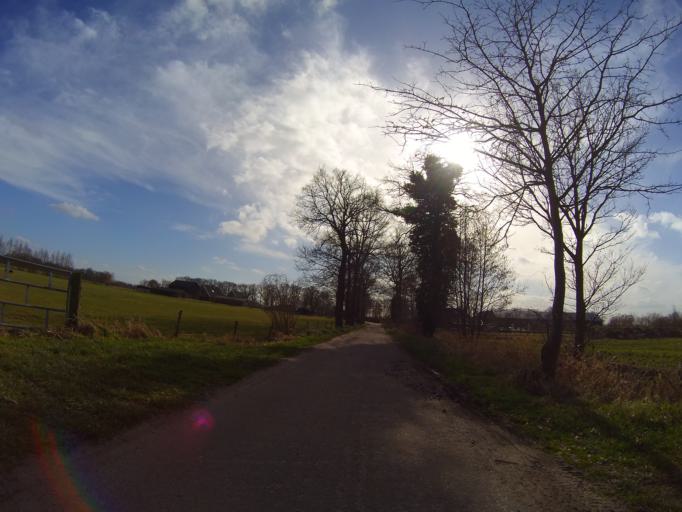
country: NL
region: Gelderland
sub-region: Gemeente Barneveld
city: Zwartebroek
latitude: 52.1514
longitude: 5.4792
